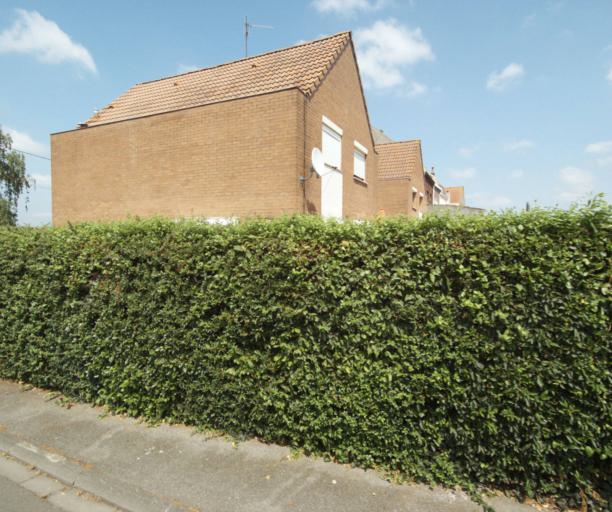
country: FR
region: Nord-Pas-de-Calais
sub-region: Departement du Nord
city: Armentieres
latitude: 50.6949
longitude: 2.8961
